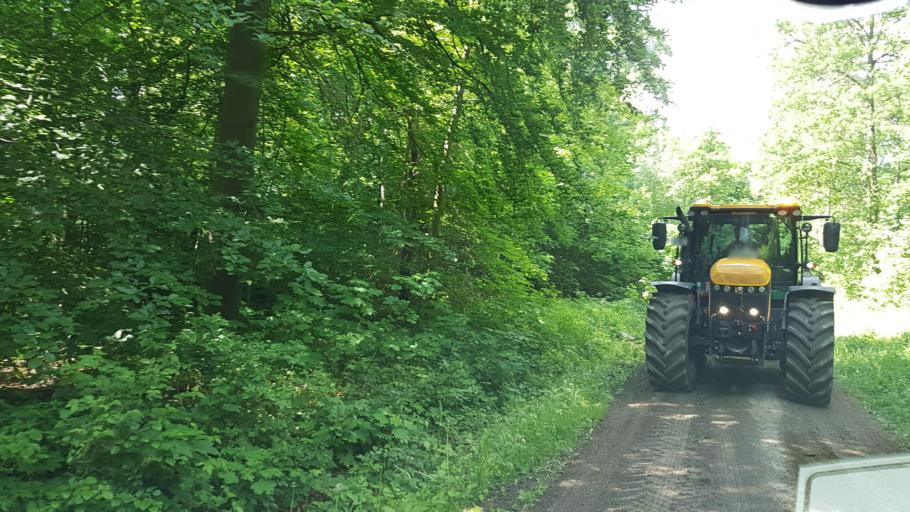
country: DE
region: Lower Saxony
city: Twieflingen
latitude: 52.1437
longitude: 10.9267
